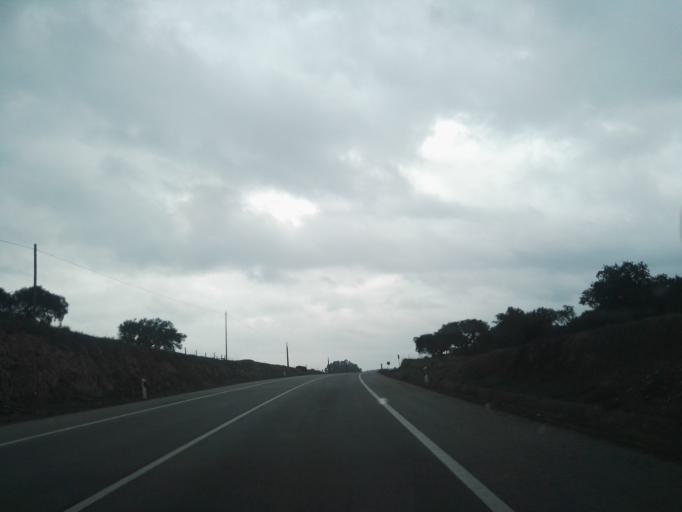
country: PT
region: Portalegre
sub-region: Portalegre
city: Alegrete
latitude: 39.1737
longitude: -7.3360
